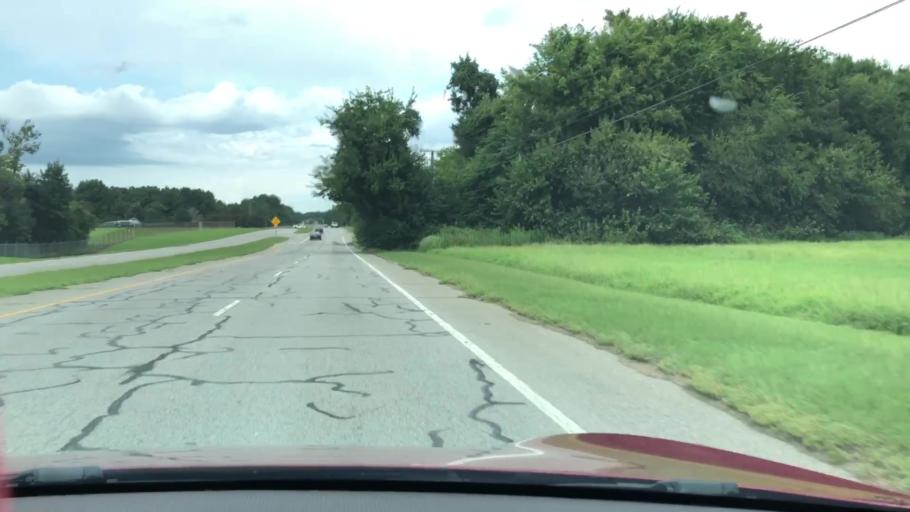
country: US
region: Virginia
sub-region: City of Virginia Beach
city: Virginia Beach
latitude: 36.8251
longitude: -76.0094
